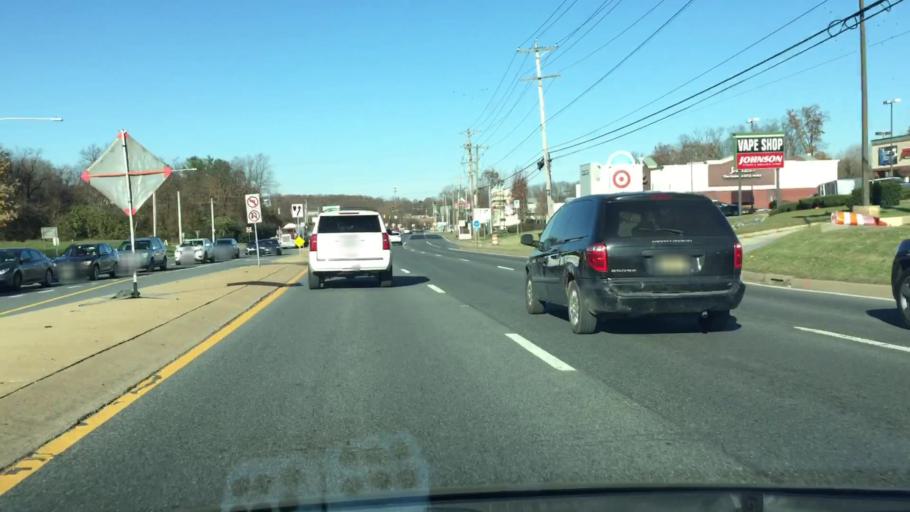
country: US
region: Delaware
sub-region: New Castle County
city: Bellefonte
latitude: 39.8298
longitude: -75.5440
